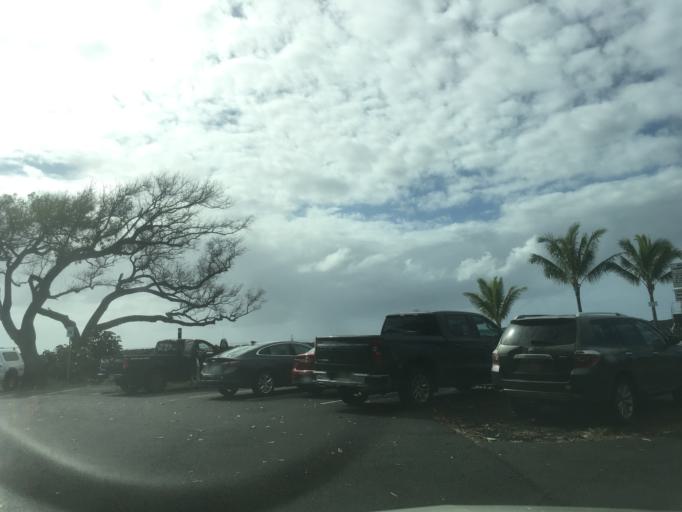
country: US
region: Hawaii
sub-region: Hawaii County
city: Leilani Estates
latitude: 19.4579
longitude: -154.8420
